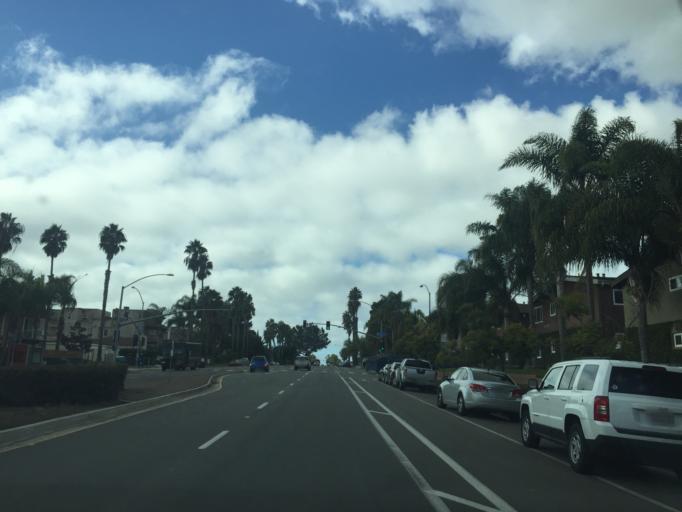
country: US
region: California
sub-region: San Diego County
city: La Jolla
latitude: 32.8005
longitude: -117.2285
